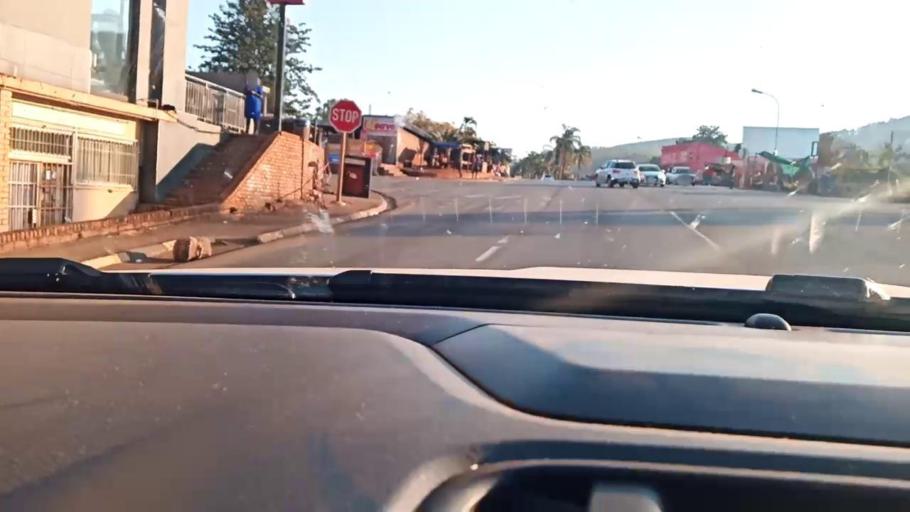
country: ZA
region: Limpopo
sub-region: Mopani District Municipality
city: Duiwelskloof
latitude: -23.6956
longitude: 30.1416
